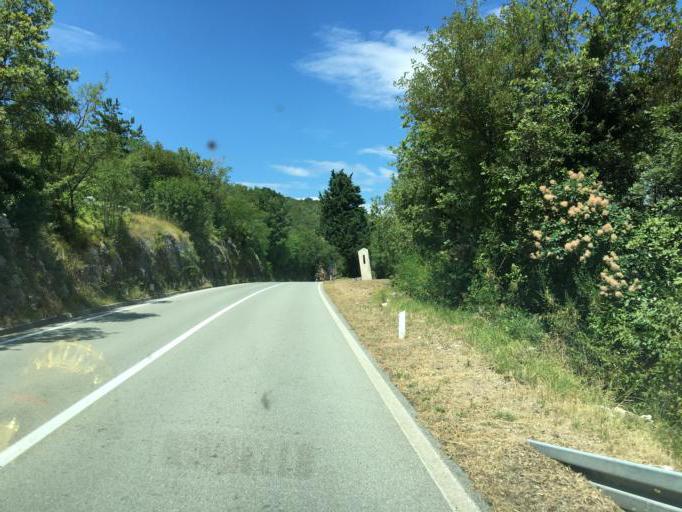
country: HR
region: Istarska
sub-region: Grad Labin
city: Rabac
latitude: 45.1648
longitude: 14.2231
